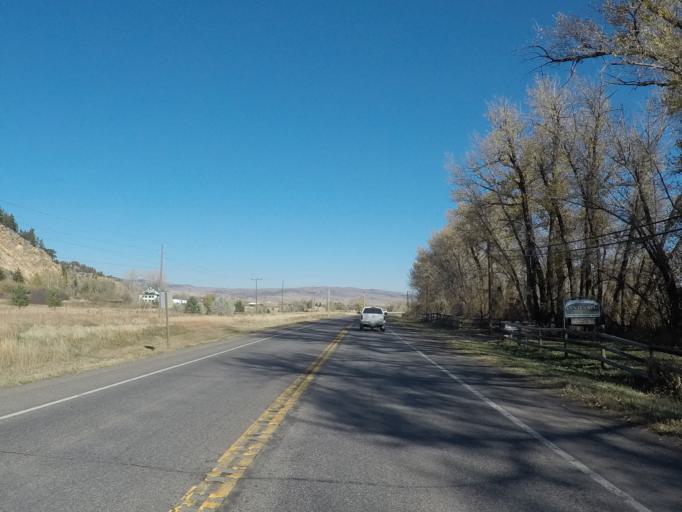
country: US
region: Montana
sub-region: Park County
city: Livingston
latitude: 45.6137
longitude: -110.5781
